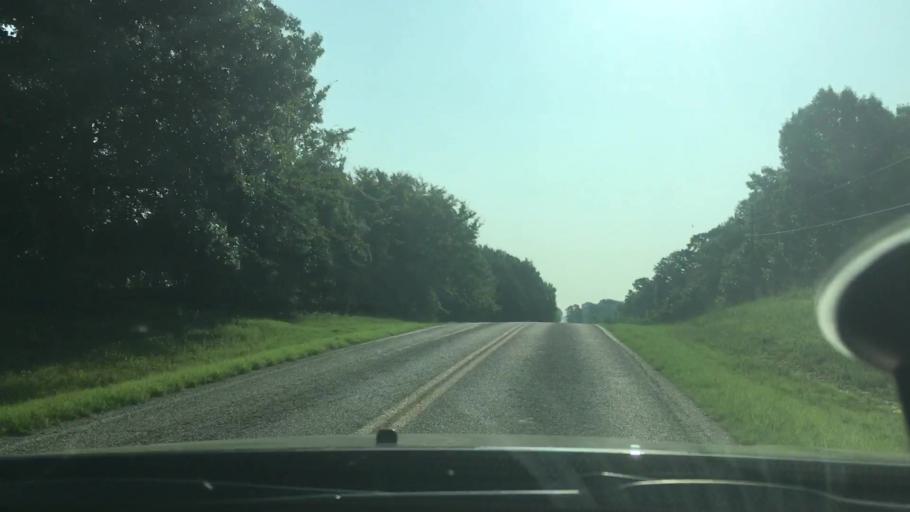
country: US
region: Oklahoma
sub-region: Johnston County
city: Tishomingo
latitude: 34.2088
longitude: -96.6291
